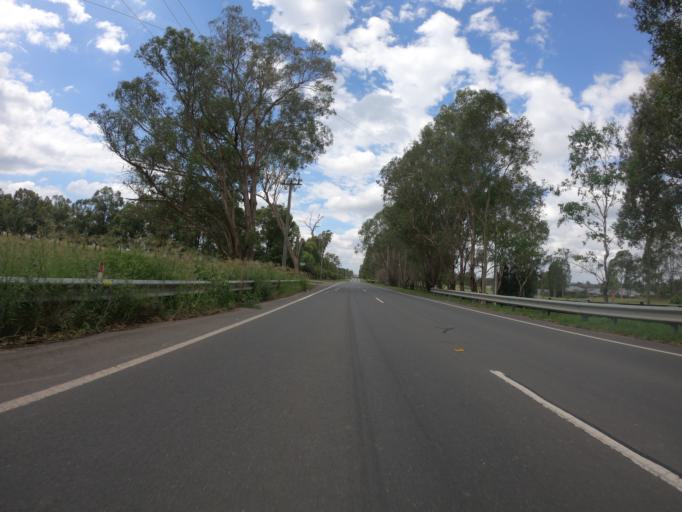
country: AU
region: New South Wales
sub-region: Liverpool
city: Luddenham
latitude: -33.8374
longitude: 150.7493
